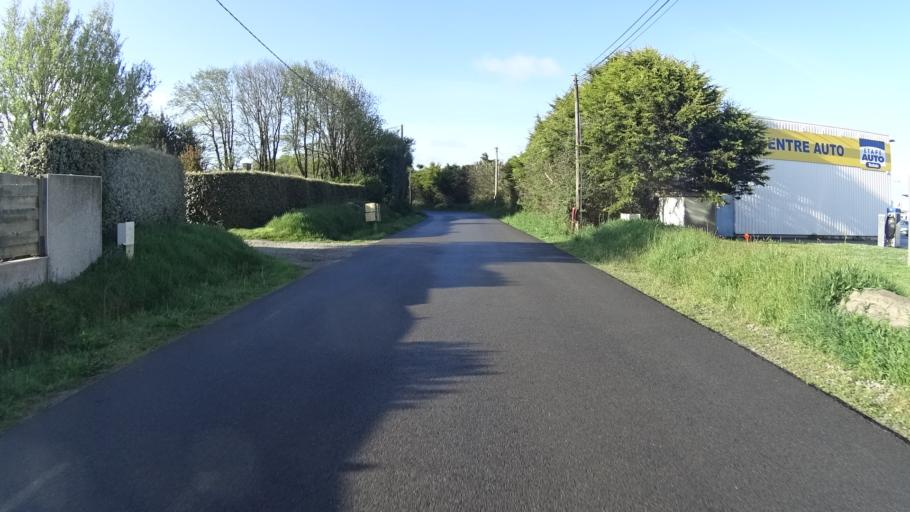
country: FR
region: Brittany
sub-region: Departement du Finistere
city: Plouarzel
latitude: 48.4334
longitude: -4.7154
